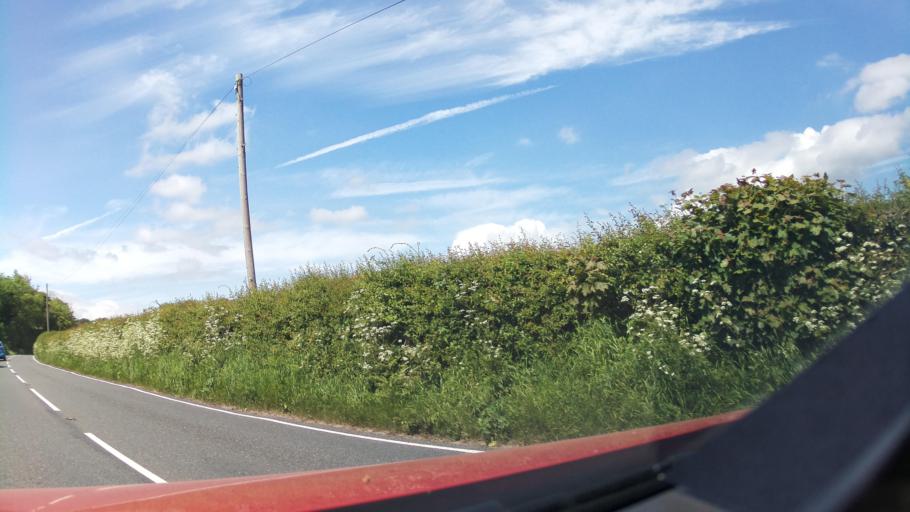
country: GB
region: Wales
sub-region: Monmouthshire
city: Mitchel Troy
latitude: 51.7670
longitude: -2.7285
